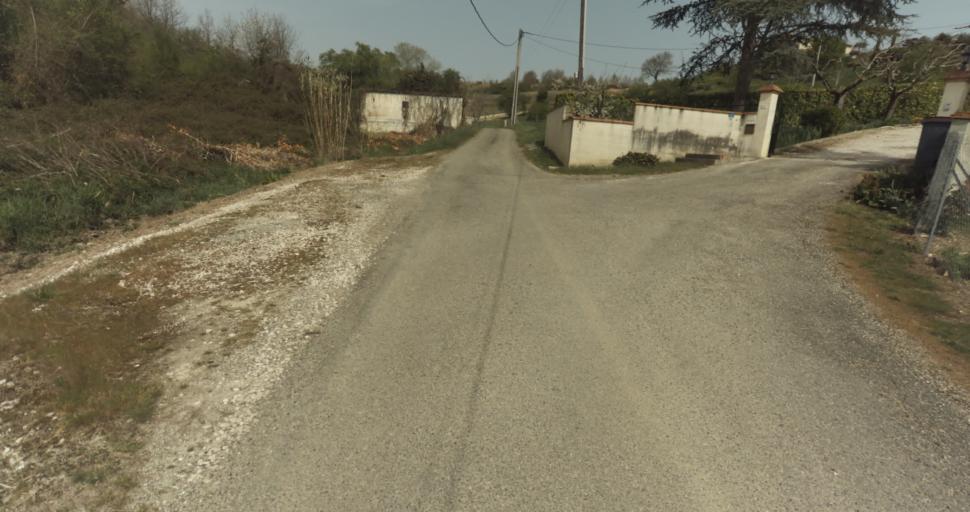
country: FR
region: Midi-Pyrenees
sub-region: Departement du Tarn-et-Garonne
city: Moissac
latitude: 44.1090
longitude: 1.0668
